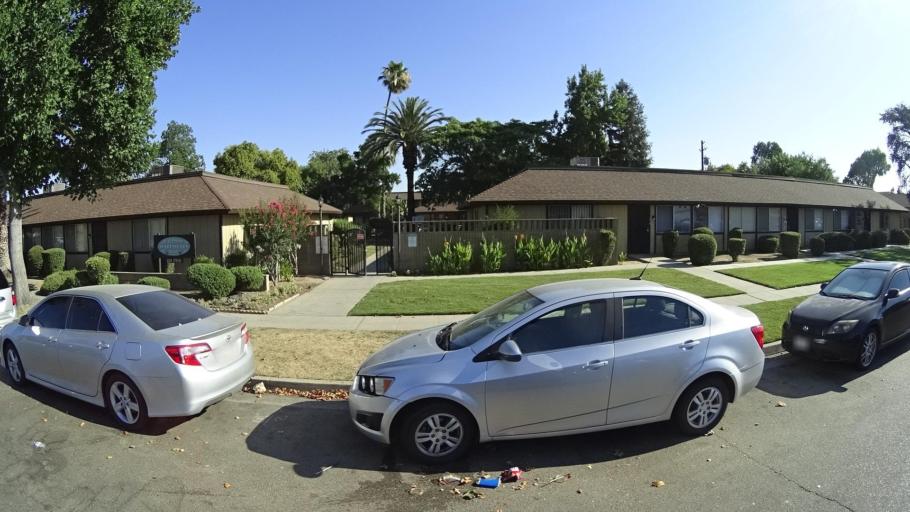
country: US
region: California
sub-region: Fresno County
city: Fresno
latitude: 36.7814
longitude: -119.7526
